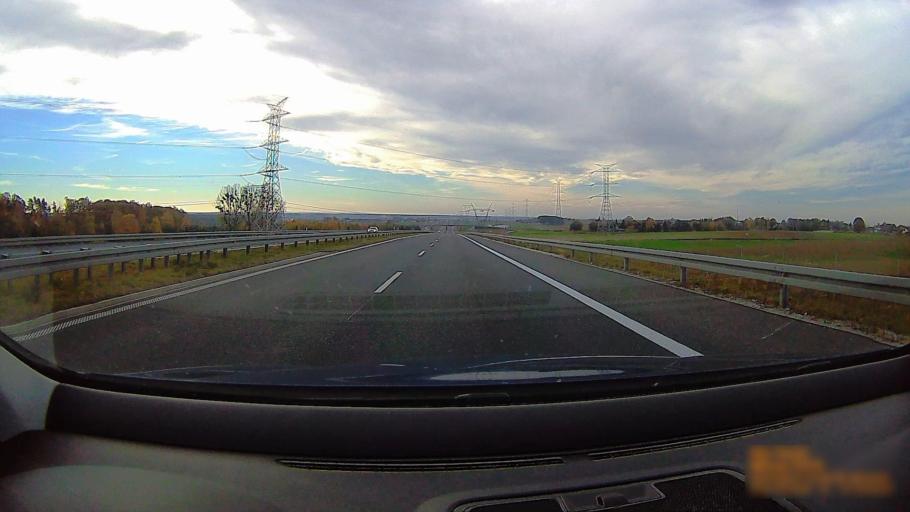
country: PL
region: Greater Poland Voivodeship
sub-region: Powiat ostrowski
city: Przygodzice
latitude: 51.6205
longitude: 17.8619
